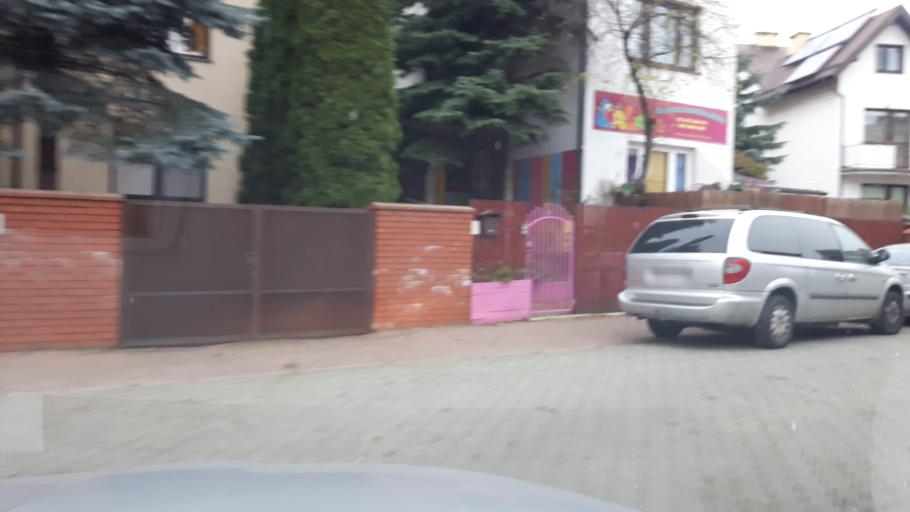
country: PL
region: Masovian Voivodeship
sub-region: Warszawa
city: Targowek
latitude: 52.2909
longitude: 21.0557
